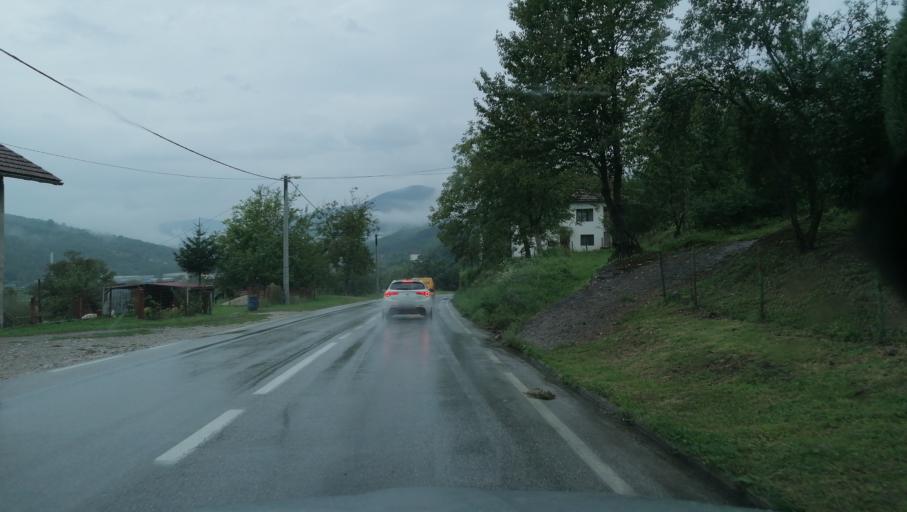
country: BA
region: Federation of Bosnia and Herzegovina
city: Gorazde
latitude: 43.6766
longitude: 19.0387
